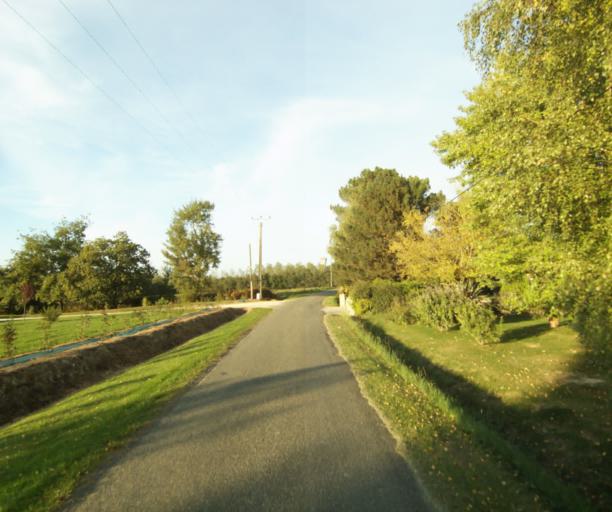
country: FR
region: Midi-Pyrenees
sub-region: Departement du Gers
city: Eauze
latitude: 43.8763
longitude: 0.0395
